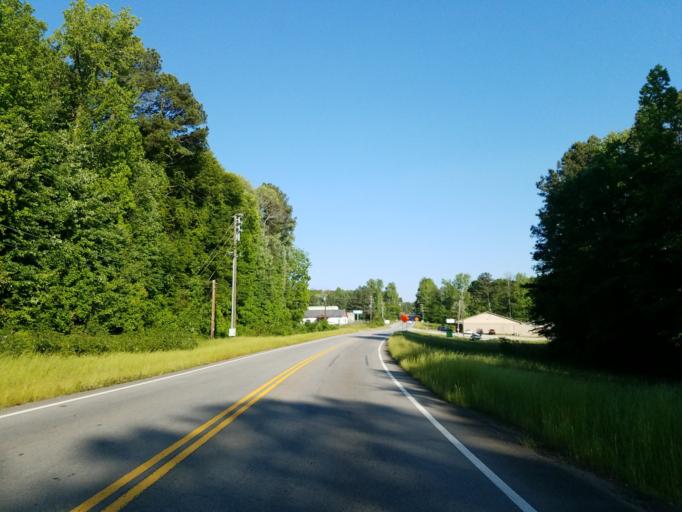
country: US
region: Georgia
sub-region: Carroll County
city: Villa Rica
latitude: 33.7310
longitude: -84.8378
